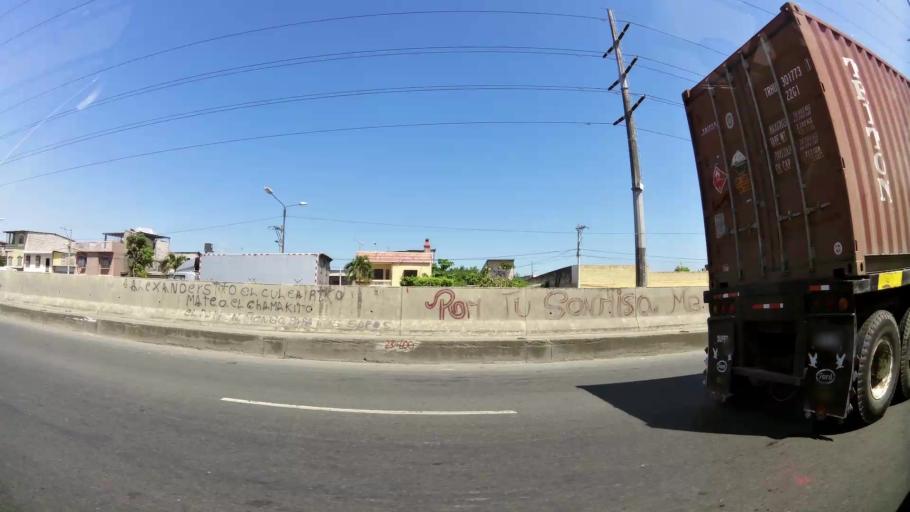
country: EC
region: Guayas
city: Guayaquil
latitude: -2.2347
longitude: -79.9364
